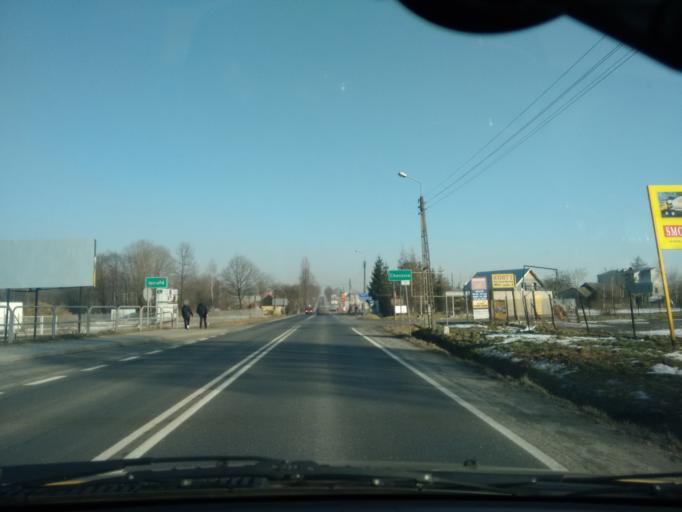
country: PL
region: Lesser Poland Voivodeship
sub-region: Powiat wadowicki
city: Chocznia
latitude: 49.8686
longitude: 19.4238
